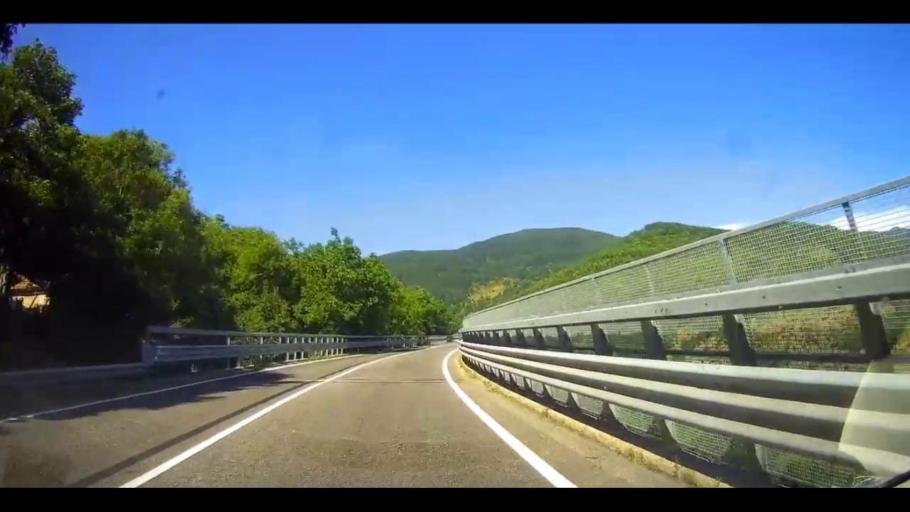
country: IT
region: Calabria
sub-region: Provincia di Cosenza
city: Spezzano Piccolo
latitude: 39.2904
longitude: 16.3491
